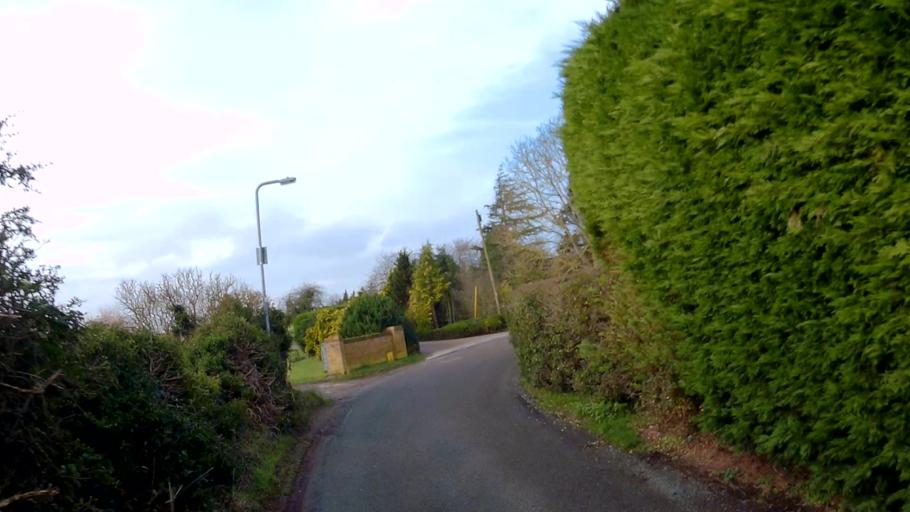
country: GB
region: England
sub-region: Lincolnshire
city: Bourne
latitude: 52.7427
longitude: -0.4193
